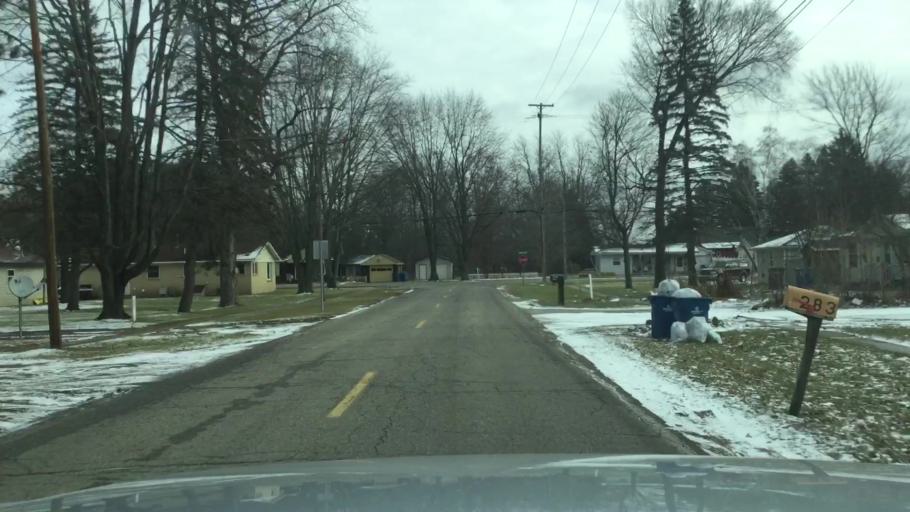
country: US
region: Michigan
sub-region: Genesee County
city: Montrose
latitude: 43.1772
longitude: -83.8861
